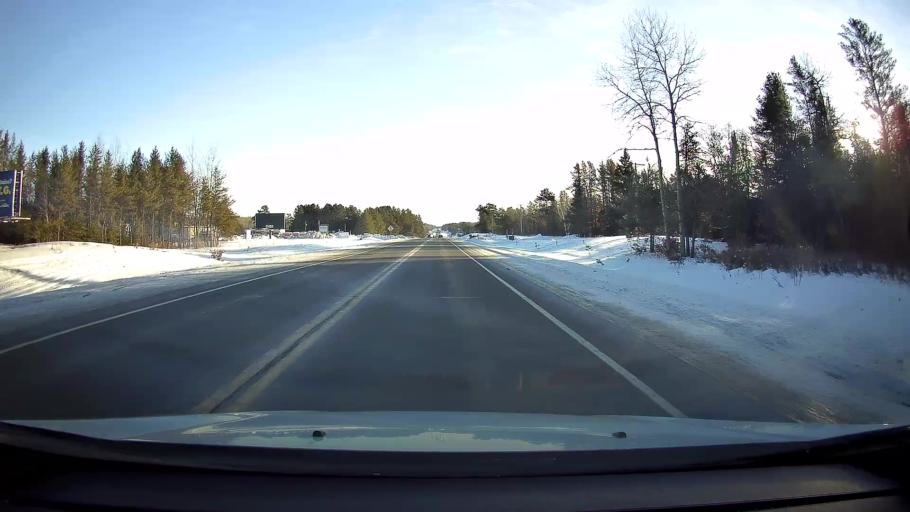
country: US
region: Wisconsin
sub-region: Washburn County
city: Spooner
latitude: 45.9104
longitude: -91.8022
